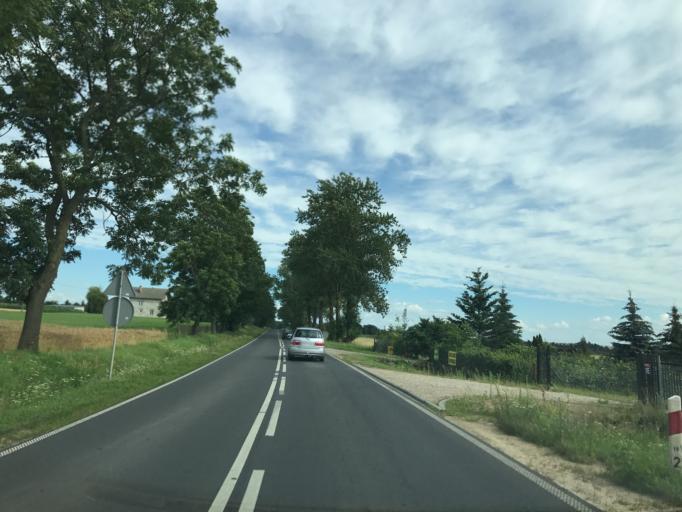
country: PL
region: Kujawsko-Pomorskie
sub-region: Powiat rypinski
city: Rypin
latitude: 53.0945
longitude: 19.3997
